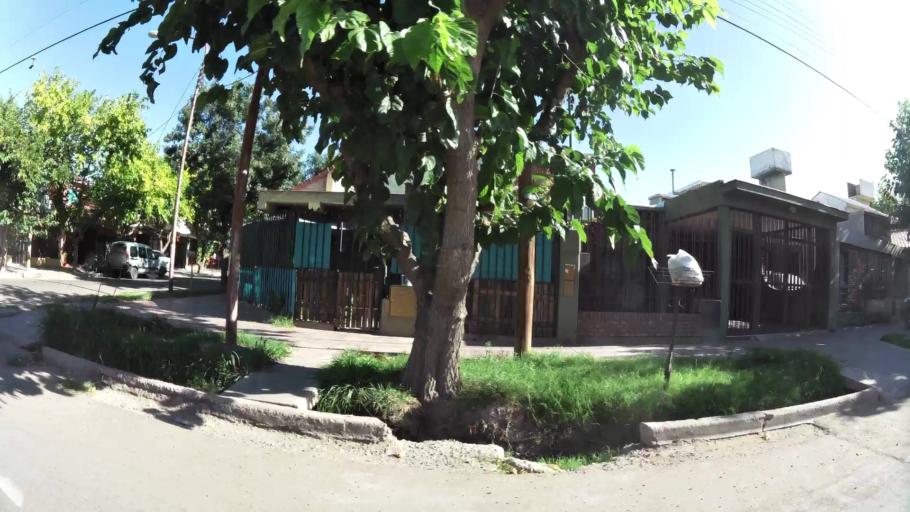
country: AR
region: Mendoza
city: Mendoza
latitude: -32.9067
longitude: -68.8162
